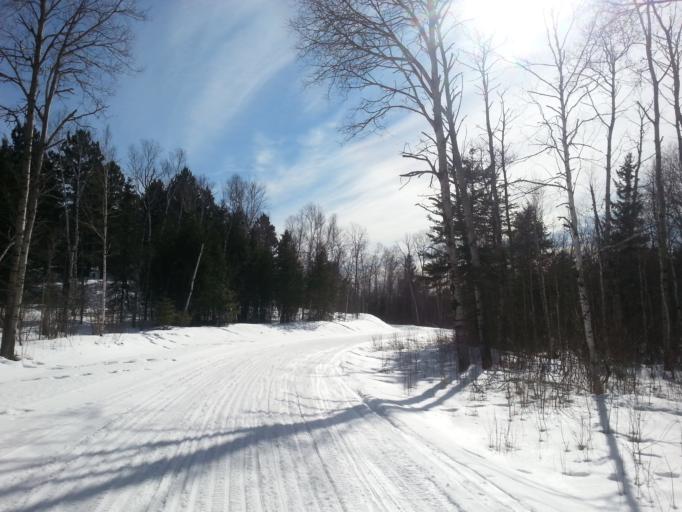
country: CA
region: Ontario
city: Greater Sudbury
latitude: 46.3338
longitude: -80.9056
